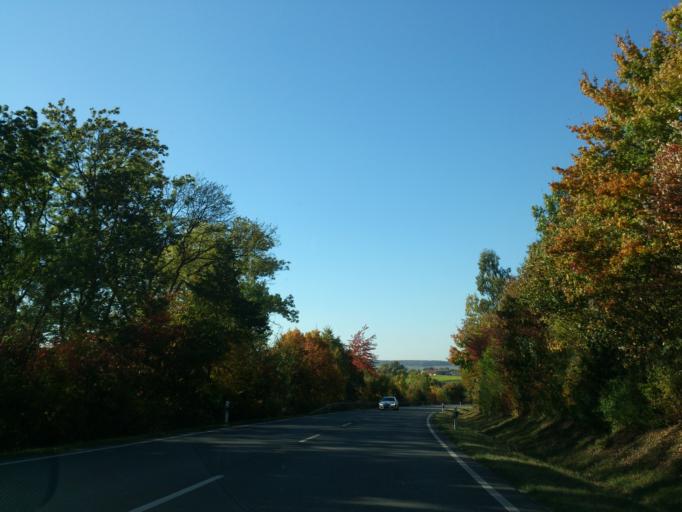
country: DE
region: Hesse
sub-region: Regierungsbezirk Kassel
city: Calden
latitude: 51.4262
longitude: 9.3472
